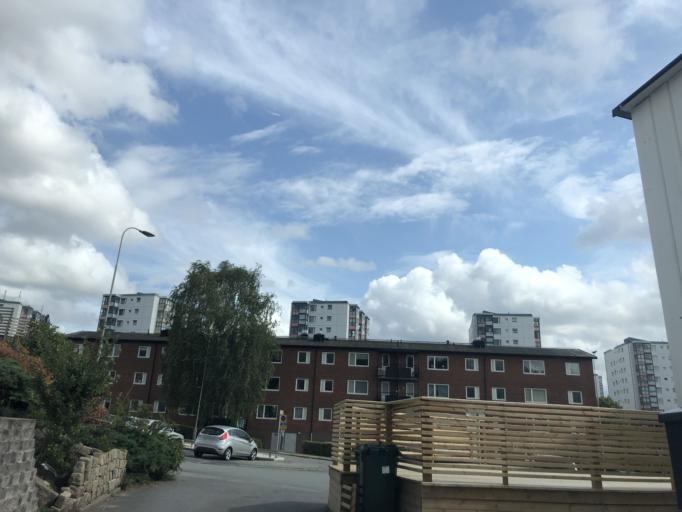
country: SE
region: Vaestra Goetaland
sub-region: Goteborg
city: Majorna
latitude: 57.7120
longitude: 11.8855
